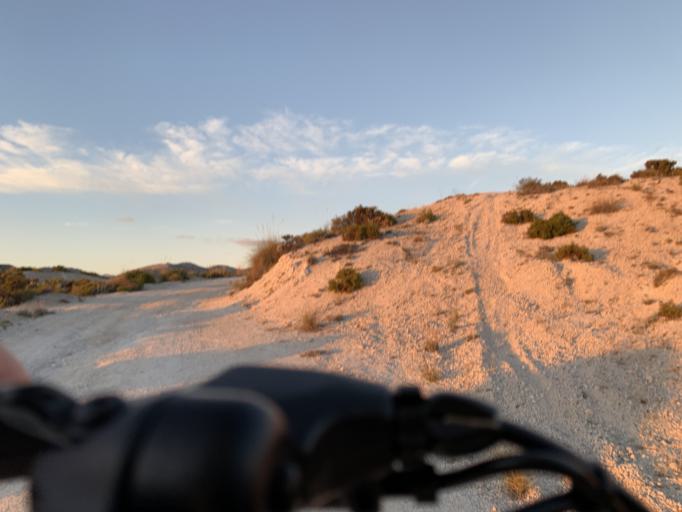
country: ES
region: Andalusia
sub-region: Provincia de Granada
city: Beas de Granada
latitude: 37.2261
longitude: -3.4668
